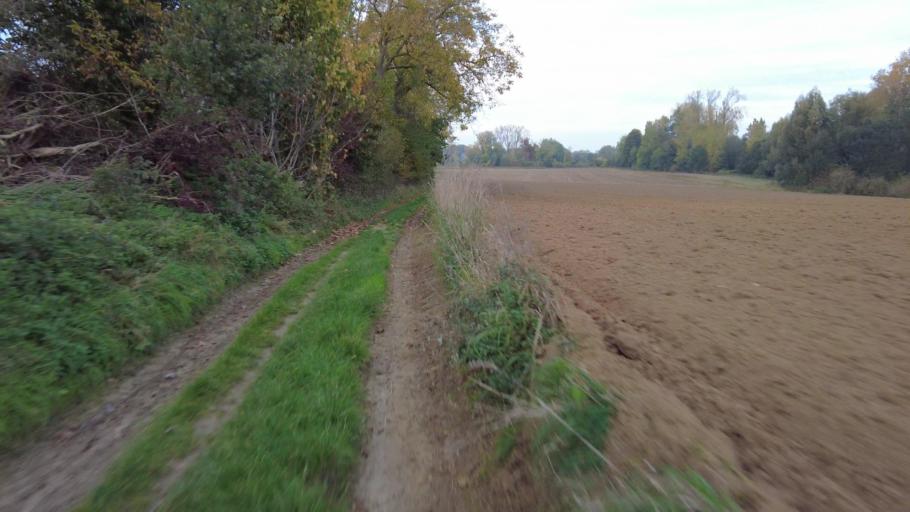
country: BE
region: Wallonia
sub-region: Province du Brabant Wallon
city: Jodoigne
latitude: 50.7367
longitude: 4.8740
